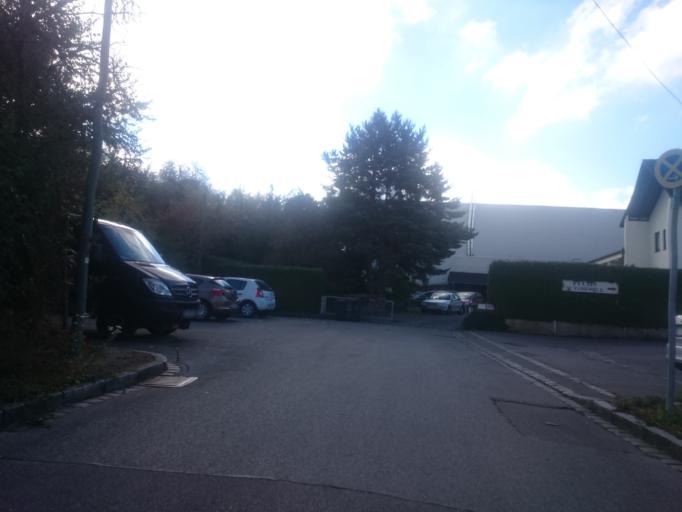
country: DE
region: Bavaria
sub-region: Swabia
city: Augsburg
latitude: 48.3773
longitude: 10.9385
